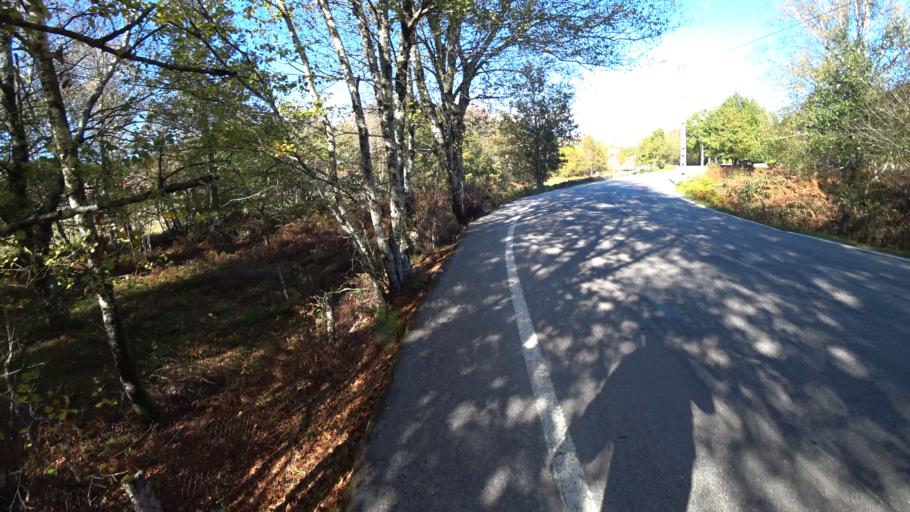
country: PT
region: Braga
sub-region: Terras de Bouro
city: Antas
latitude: 41.7565
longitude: -8.1935
